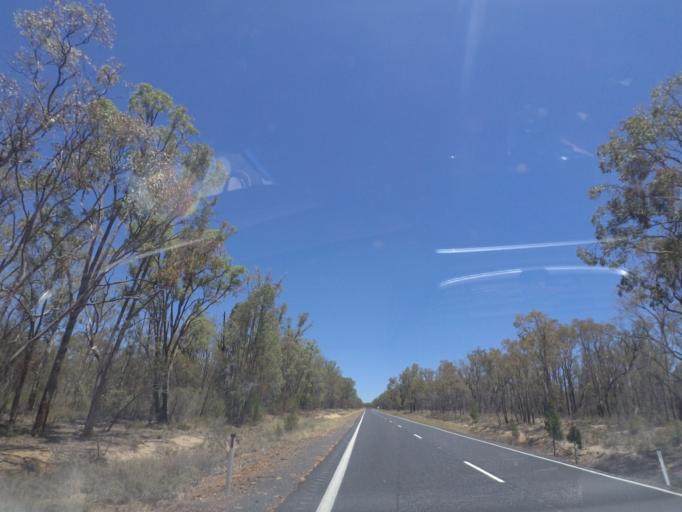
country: AU
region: New South Wales
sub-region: Warrumbungle Shire
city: Coonabarabran
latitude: -31.1680
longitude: 149.3628
